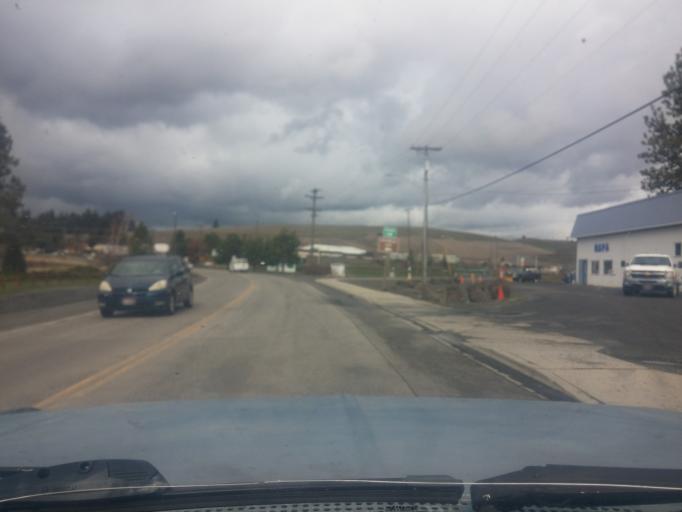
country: US
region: Idaho
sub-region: Latah County
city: Moscow
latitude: 46.9242
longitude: -116.9023
